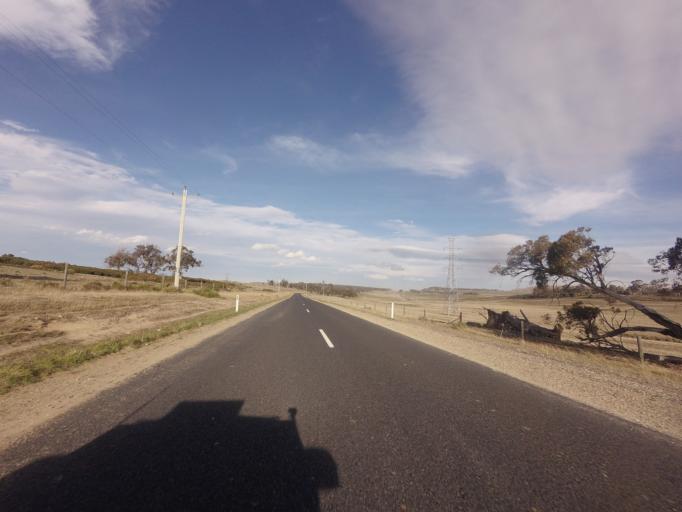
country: AU
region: Tasmania
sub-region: Derwent Valley
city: New Norfolk
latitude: -42.2559
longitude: 146.9349
